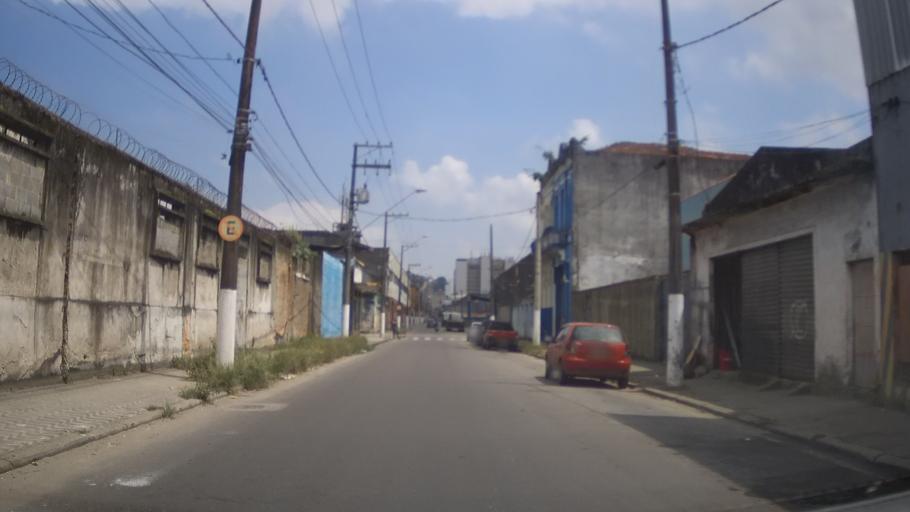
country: BR
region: Sao Paulo
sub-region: Santos
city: Santos
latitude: -23.9351
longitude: -46.3187
